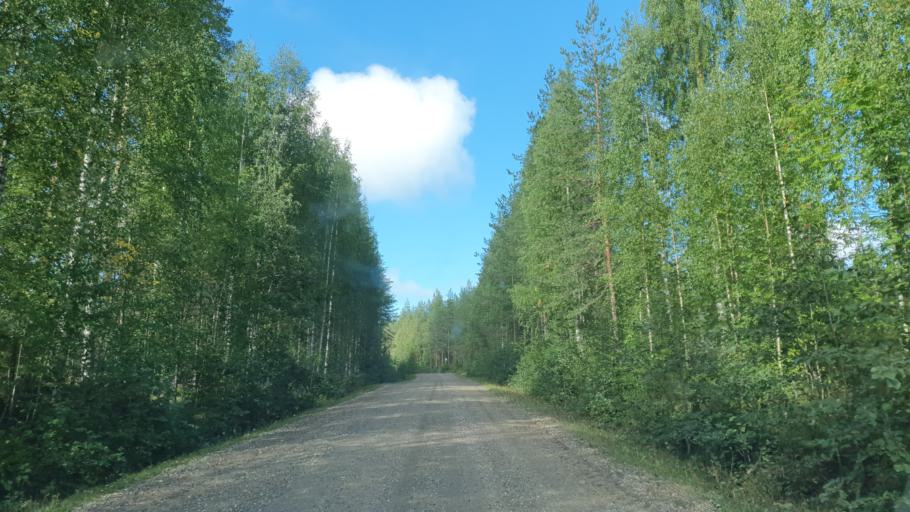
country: FI
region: Kainuu
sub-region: Kehys-Kainuu
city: Kuhmo
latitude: 64.0377
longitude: 29.1466
